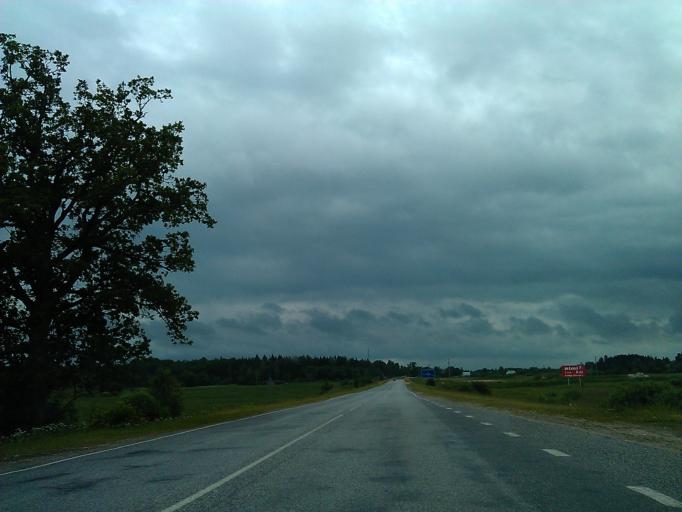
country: LV
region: Kuldigas Rajons
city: Kuldiga
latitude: 56.9778
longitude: 22.0162
